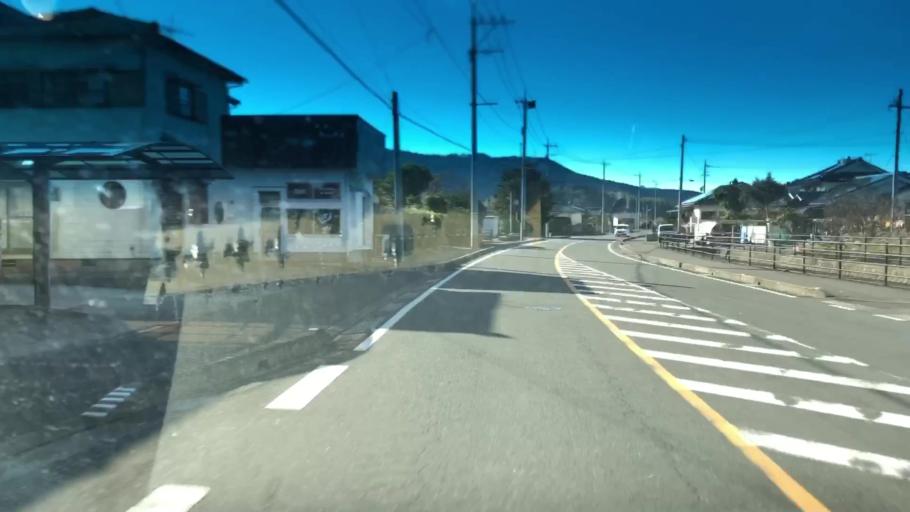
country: JP
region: Kagoshima
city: Satsumasendai
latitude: 31.8167
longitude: 130.2858
